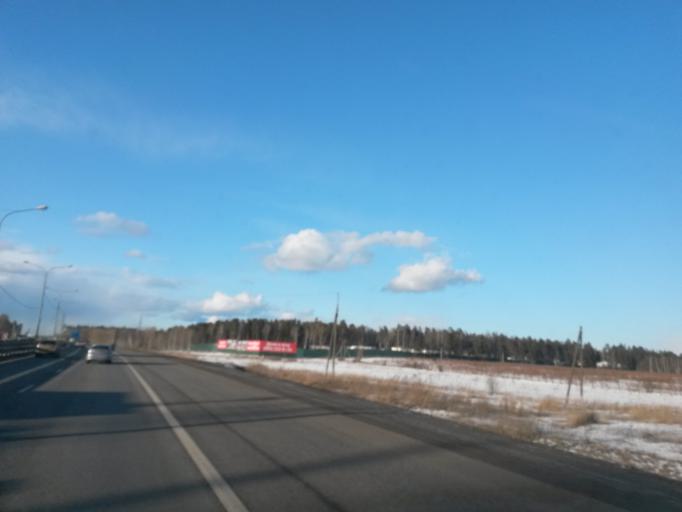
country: RU
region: Moskovskaya
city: Pushkino
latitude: 56.0017
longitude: 37.8778
